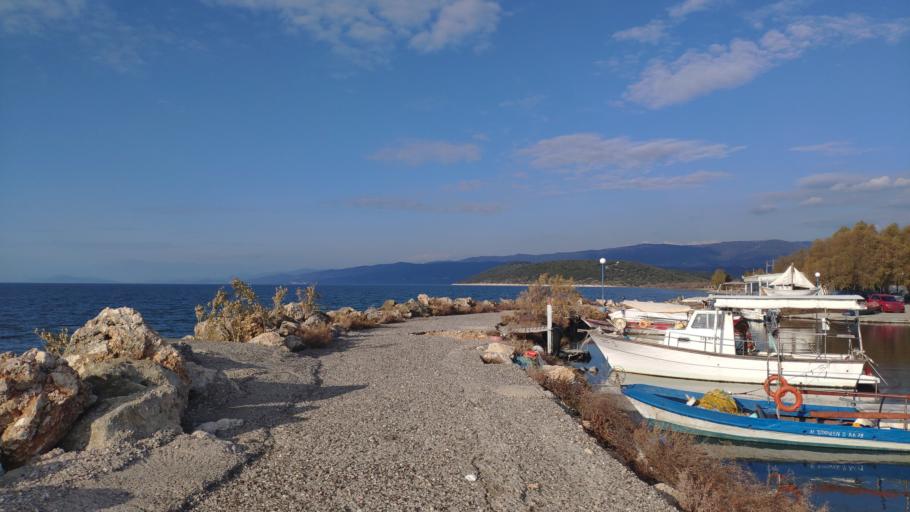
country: GR
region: West Greece
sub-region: Nomos Aitolias kai Akarnanias
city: Krikellos
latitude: 38.9271
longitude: 21.1395
